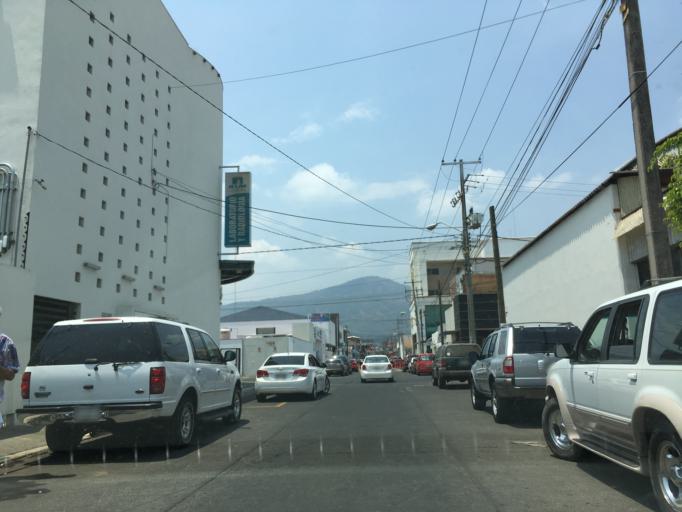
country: MX
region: Michoacan
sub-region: Uruapan
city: Uruapan
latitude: 19.4113
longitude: -102.0538
